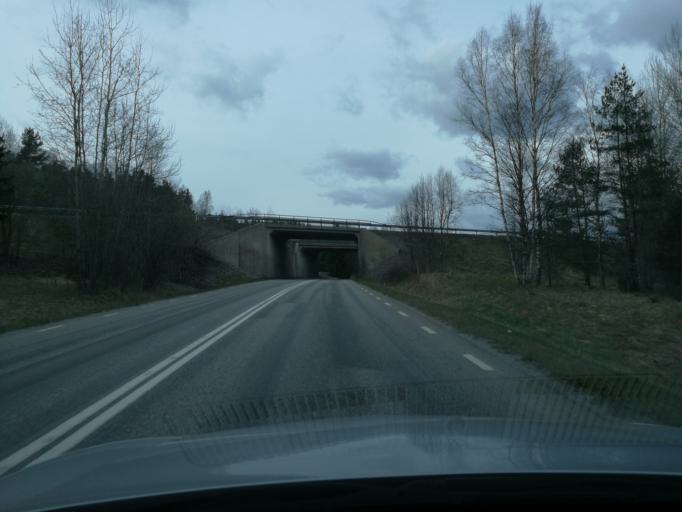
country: SE
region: Soedermanland
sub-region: Gnesta Kommun
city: Gnesta
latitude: 58.9064
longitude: 17.3254
